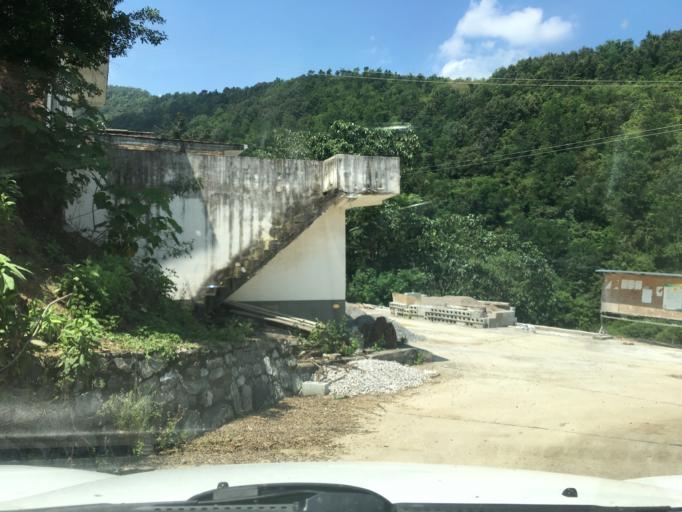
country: CN
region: Guangxi Zhuangzu Zizhiqu
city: Xinzhou
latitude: 25.4601
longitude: 105.7691
